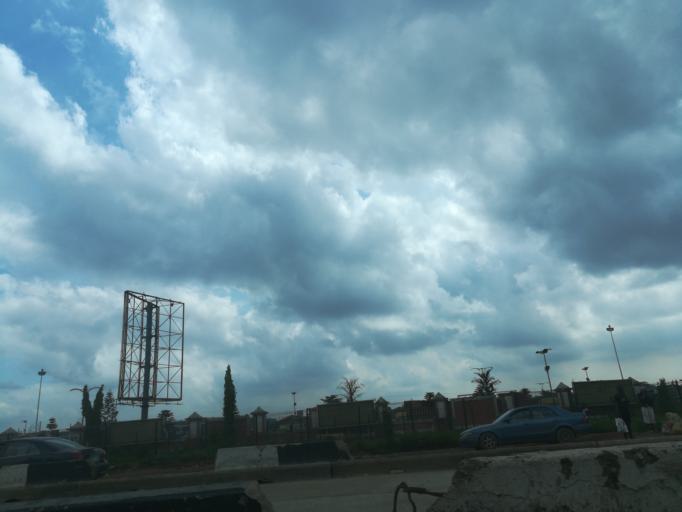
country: NG
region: Lagos
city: Oshodi
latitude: 6.5630
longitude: 3.3487
